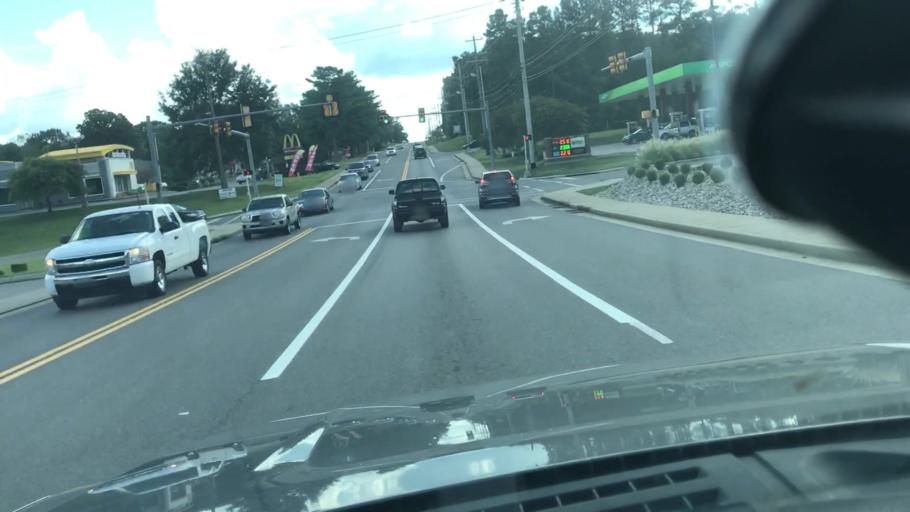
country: US
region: Tennessee
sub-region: Williamson County
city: Fairview
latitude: 35.9735
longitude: -87.1284
